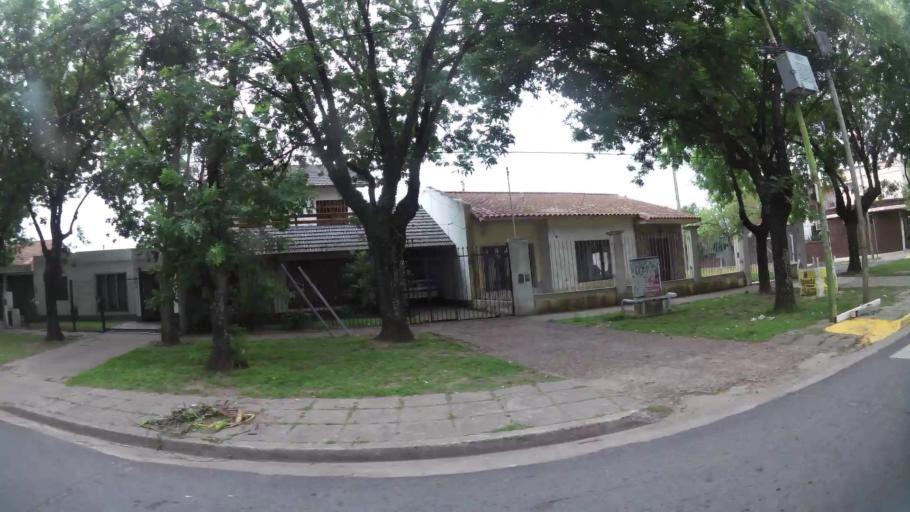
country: AR
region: Buenos Aires
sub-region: Partido de Campana
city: Campana
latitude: -34.1625
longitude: -58.9734
